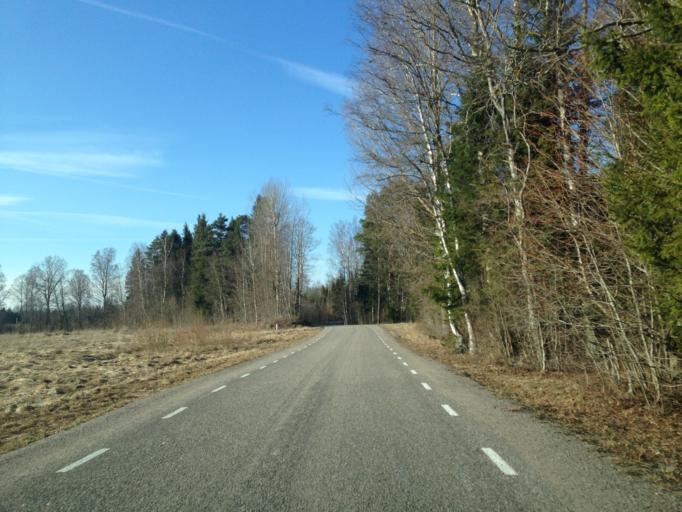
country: EE
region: Harju
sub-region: Nissi vald
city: Turba
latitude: 59.1482
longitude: 24.1514
